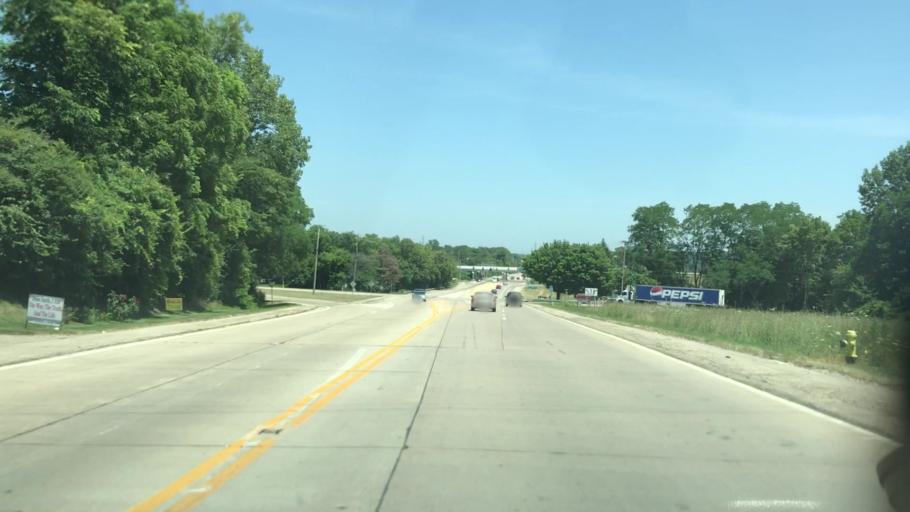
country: US
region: Ohio
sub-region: Greene County
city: Fairborn
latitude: 39.8435
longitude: -83.9982
